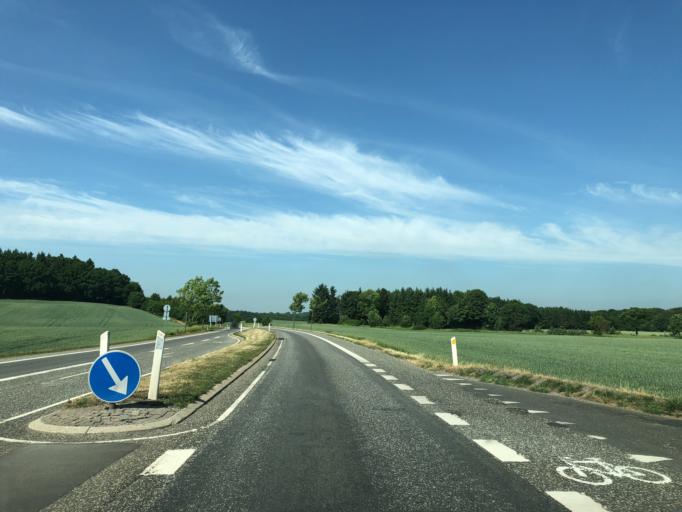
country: DK
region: South Denmark
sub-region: Vejle Kommune
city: Jelling
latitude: 55.7126
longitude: 9.3701
